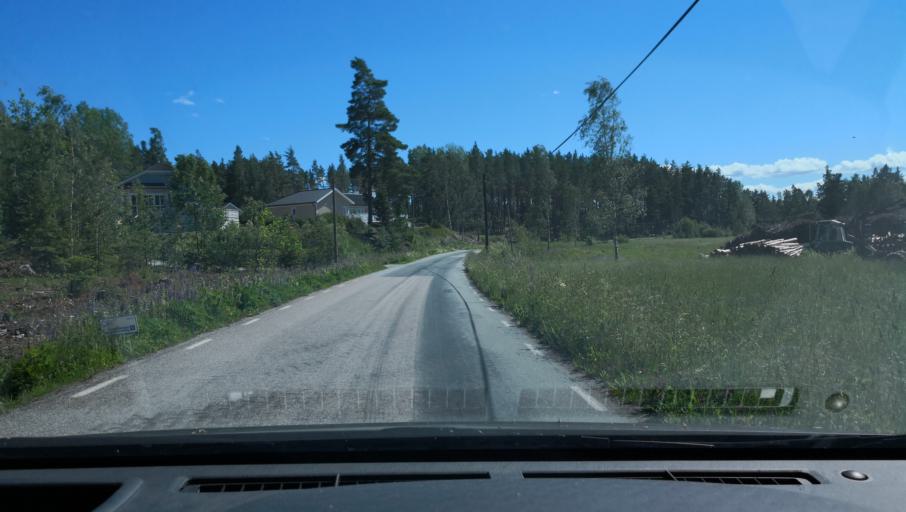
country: SE
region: Soedermanland
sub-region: Eskilstuna Kommun
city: Hallbybrunn
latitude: 59.3159
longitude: 16.3783
